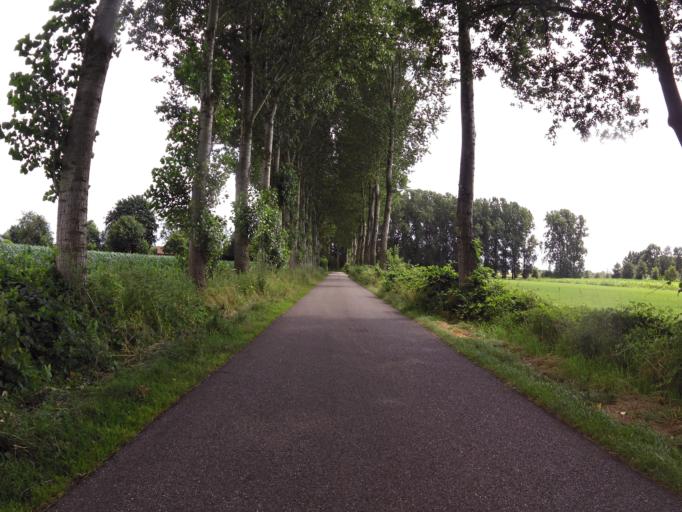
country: NL
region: North Brabant
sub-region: Gemeente Sint-Oedenrode
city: Sint-Oedenrode
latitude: 51.5758
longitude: 5.4807
